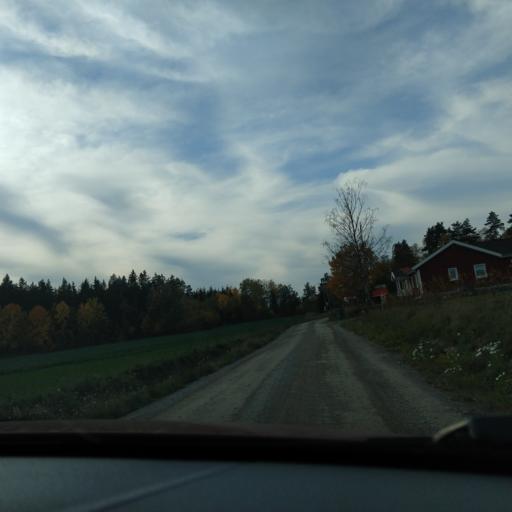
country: SE
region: Stockholm
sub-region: Vallentuna Kommun
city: Vallentuna
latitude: 59.5328
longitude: 18.0121
